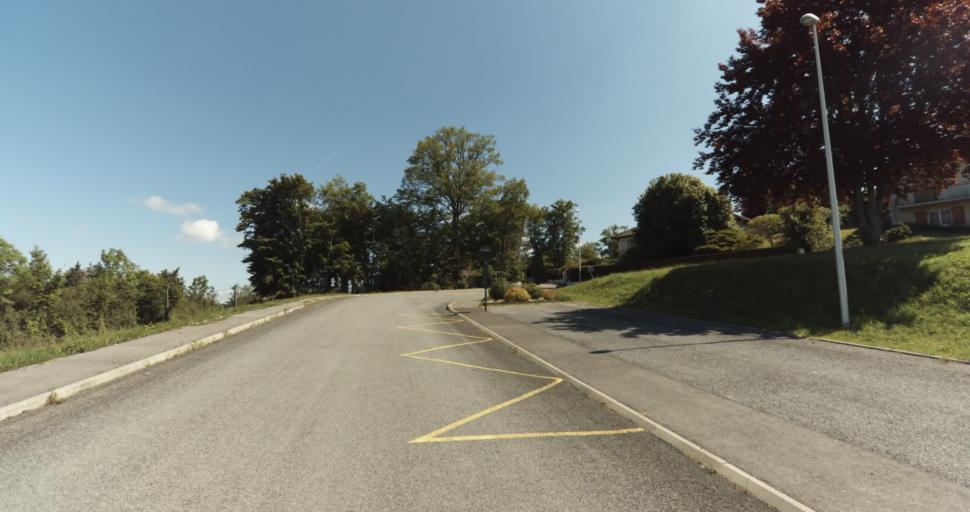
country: FR
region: Limousin
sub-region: Departement de la Haute-Vienne
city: Le Vigen
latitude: 45.7391
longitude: 1.2855
